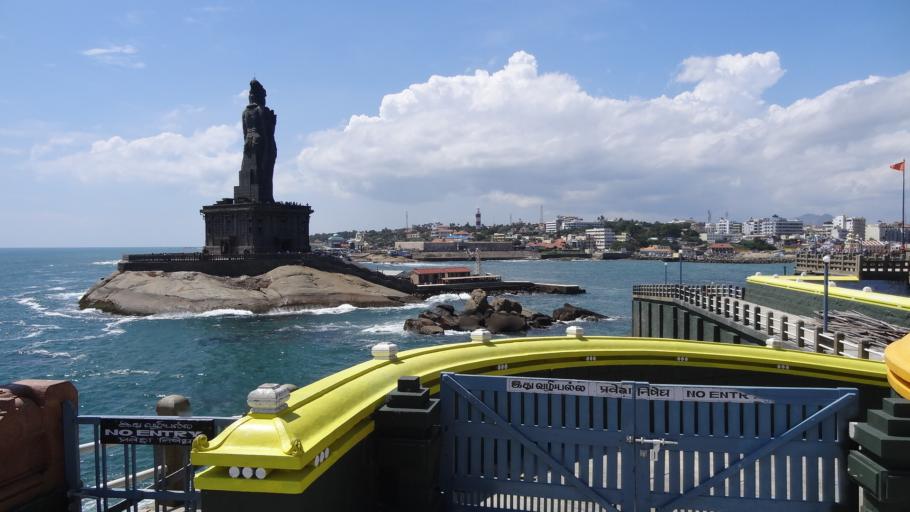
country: IN
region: Tamil Nadu
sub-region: Kanniyakumari
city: Kanniyakumari
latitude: 8.0776
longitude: 77.5555
